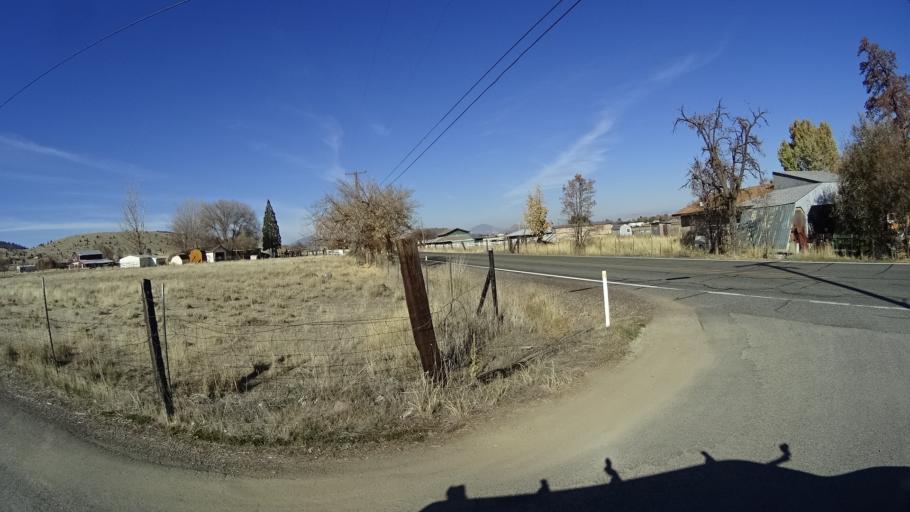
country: US
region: California
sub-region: Siskiyou County
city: Montague
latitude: 41.6327
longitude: -122.5302
